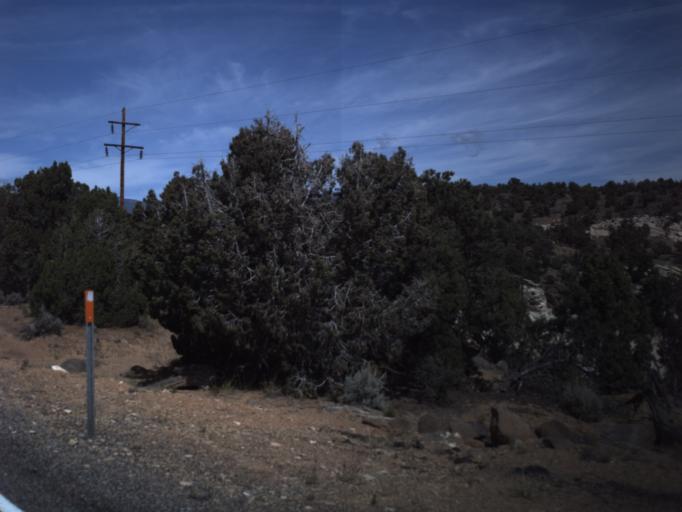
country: US
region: Utah
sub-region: Wayne County
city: Loa
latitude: 37.8619
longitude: -111.4384
